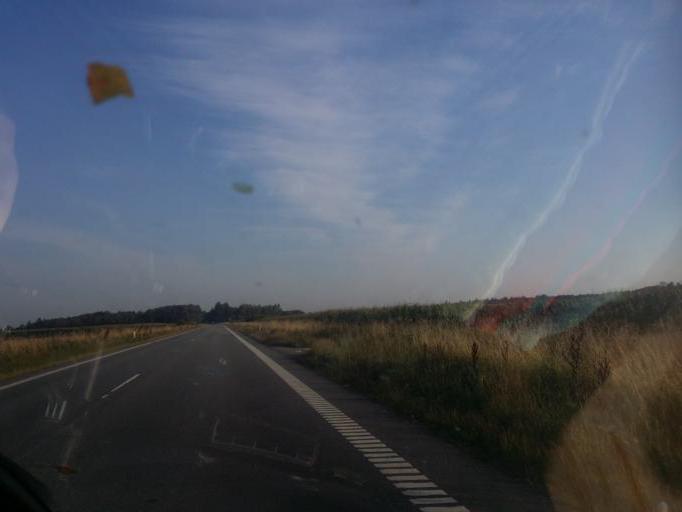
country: DK
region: South Denmark
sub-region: Tonder Kommune
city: Tonder
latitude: 55.0030
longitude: 8.8546
